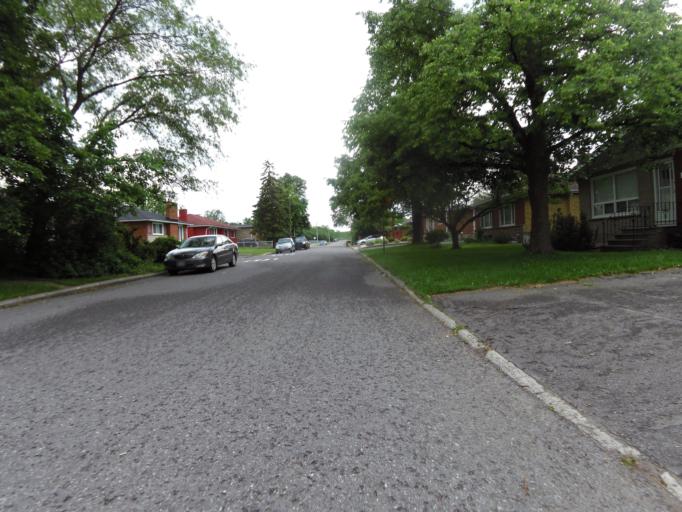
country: CA
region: Ontario
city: Ottawa
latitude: 45.3736
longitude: -75.7383
